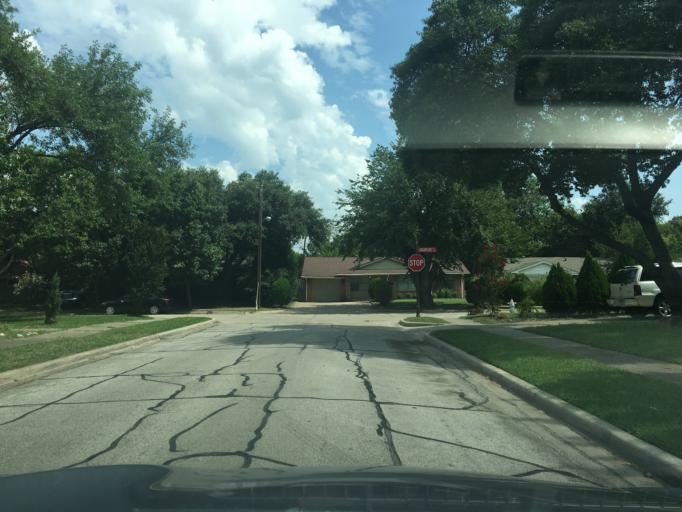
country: US
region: Texas
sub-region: Dallas County
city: Farmers Branch
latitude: 32.9296
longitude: -96.8711
